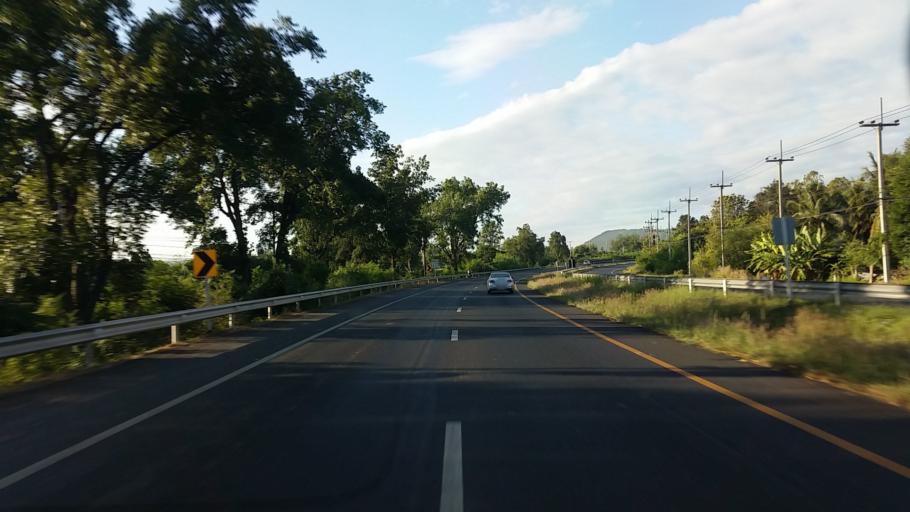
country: TH
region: Lop Buri
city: Phatthana Nikhom
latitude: 14.9919
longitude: 100.9342
